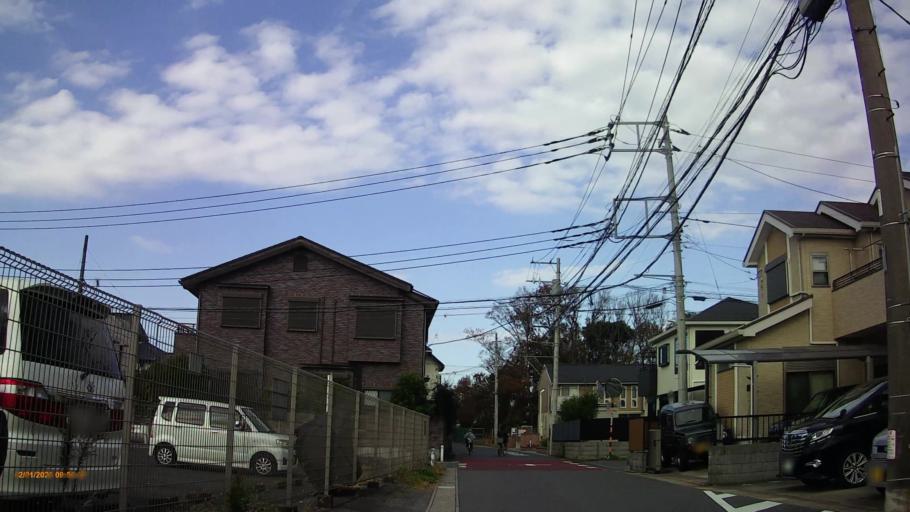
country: JP
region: Chiba
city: Yotsukaido
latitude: 35.6313
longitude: 140.1800
